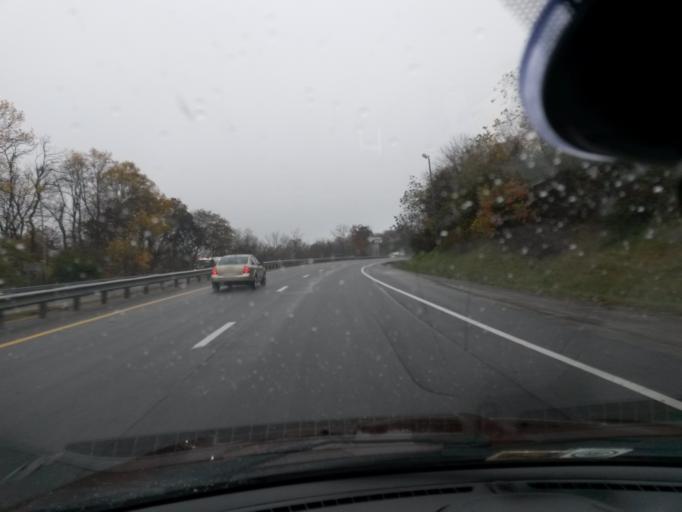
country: US
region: Virginia
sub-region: Montgomery County
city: Christiansburg
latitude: 37.1520
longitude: -80.4041
